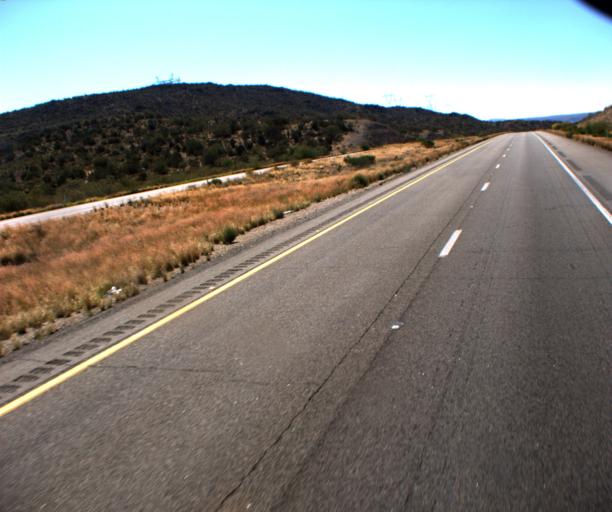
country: US
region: Arizona
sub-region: Yavapai County
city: Bagdad
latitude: 34.4218
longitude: -113.2386
